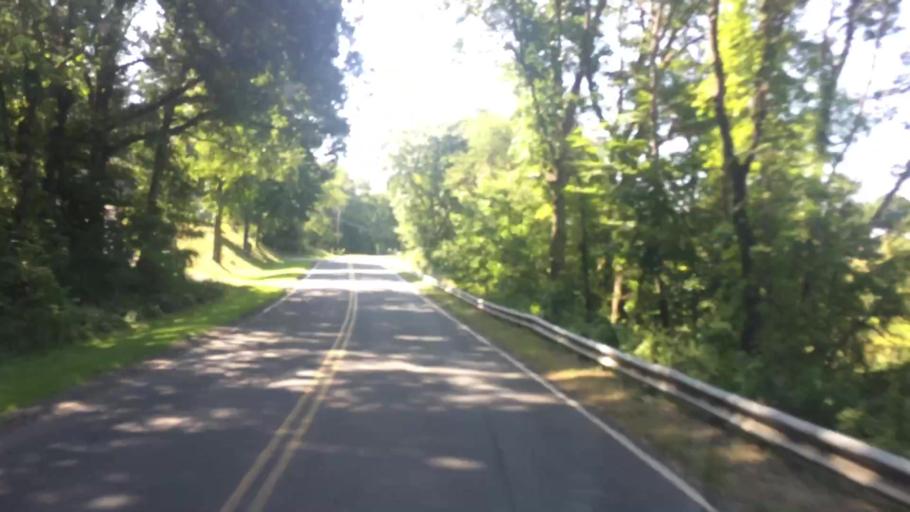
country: US
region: Massachusetts
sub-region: Hampshire County
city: Granby
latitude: 42.2544
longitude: -72.5422
